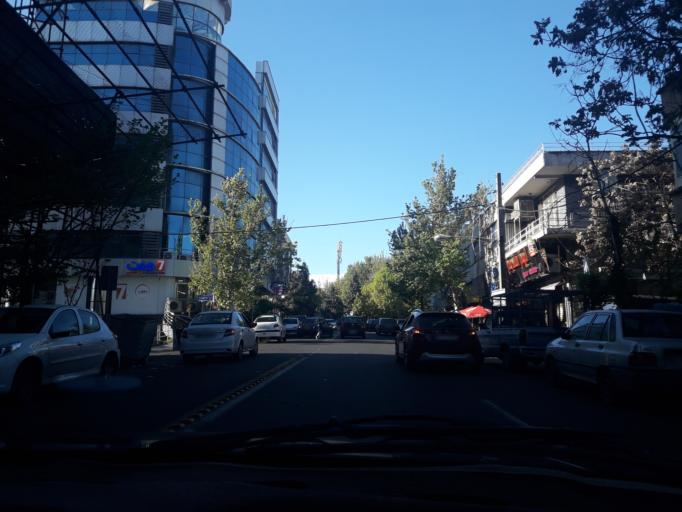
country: IR
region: Tehran
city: Tehran
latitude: 35.7221
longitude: 51.4025
